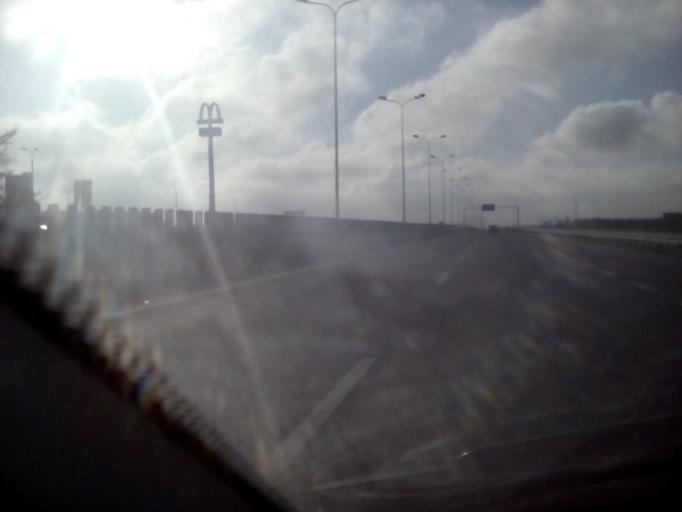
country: PL
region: Masovian Voivodeship
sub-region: Powiat grojecki
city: Goszczyn
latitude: 51.7456
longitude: 20.9103
